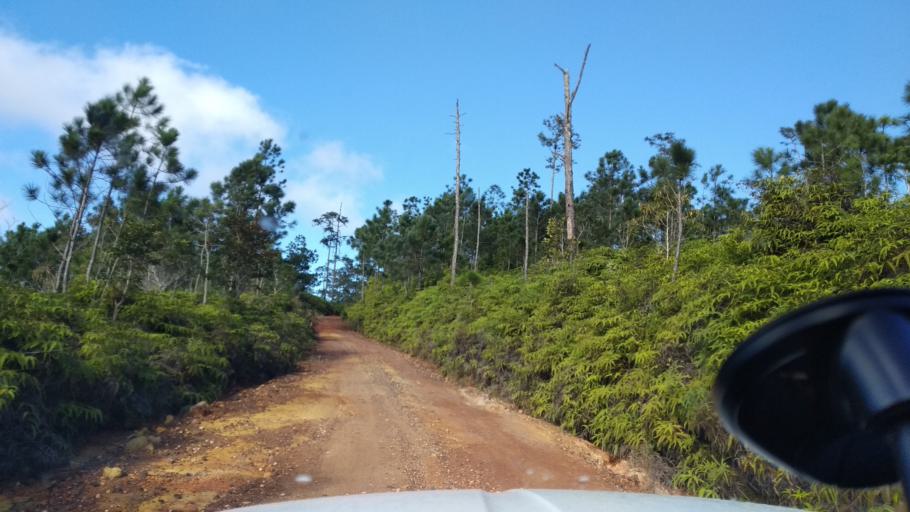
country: BZ
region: Cayo
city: Belmopan
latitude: 16.9980
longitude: -88.8307
